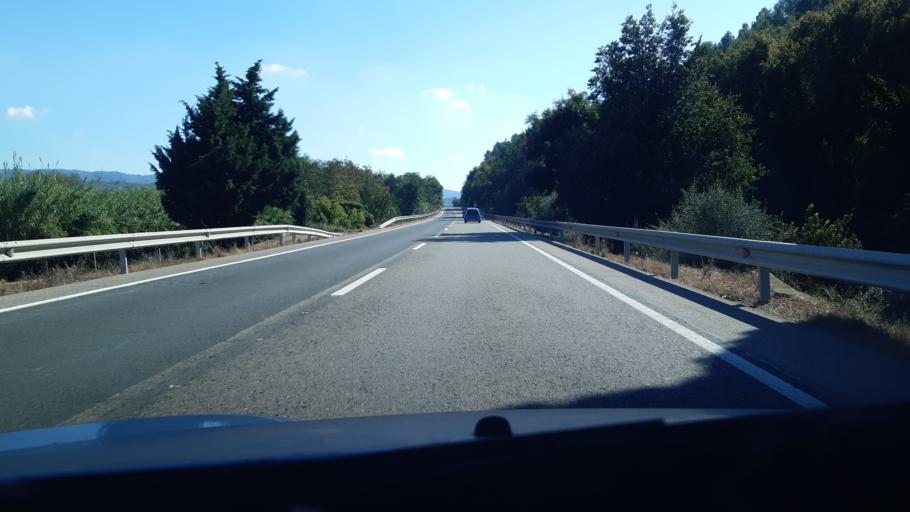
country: ES
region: Catalonia
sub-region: Provincia de Tarragona
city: Tivenys
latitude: 40.8654
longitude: 0.5056
